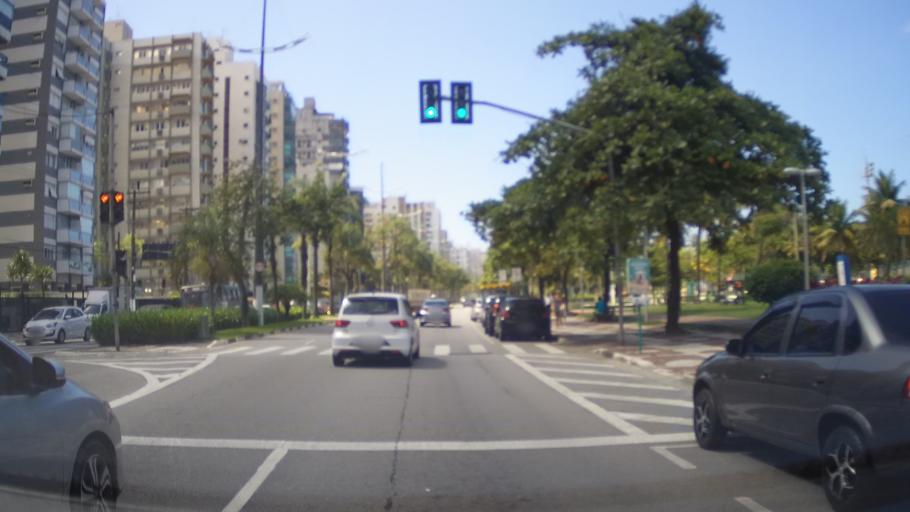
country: BR
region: Sao Paulo
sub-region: Santos
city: Santos
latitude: -23.9795
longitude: -46.3137
